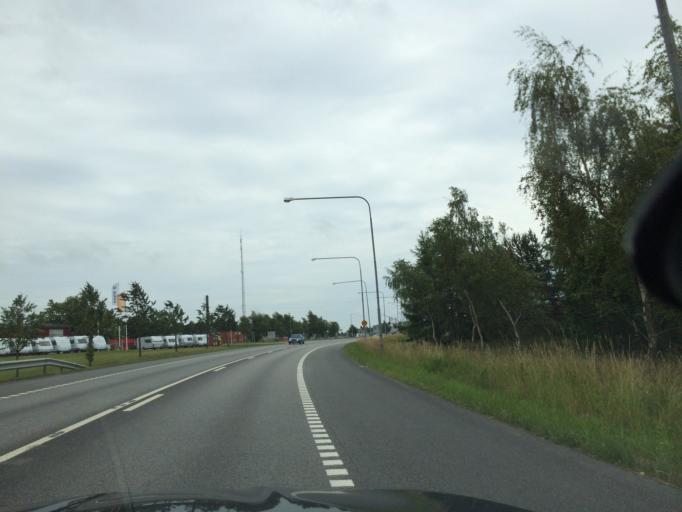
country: SE
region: Skane
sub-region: Tomelilla Kommun
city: Tomelilla
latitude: 55.5471
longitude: 13.9654
